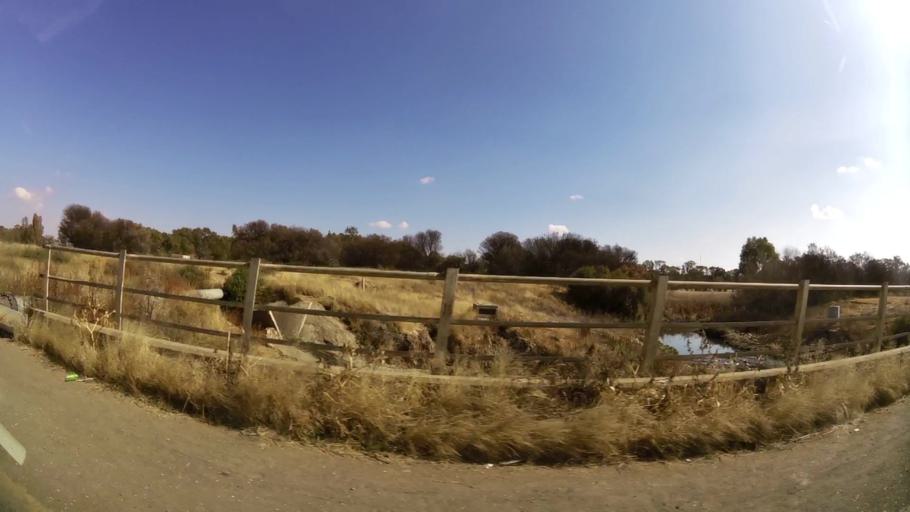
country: ZA
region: Orange Free State
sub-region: Mangaung Metropolitan Municipality
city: Bloemfontein
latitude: -29.1215
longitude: 26.2671
